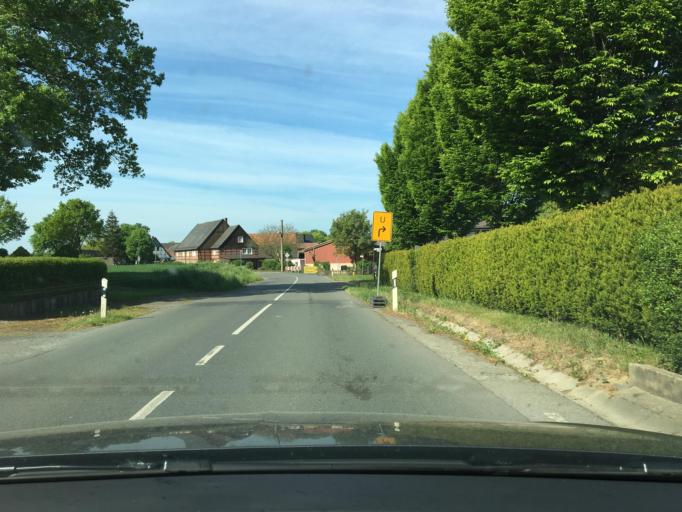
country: DE
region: North Rhine-Westphalia
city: Wickede
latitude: 51.4944
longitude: 7.8289
